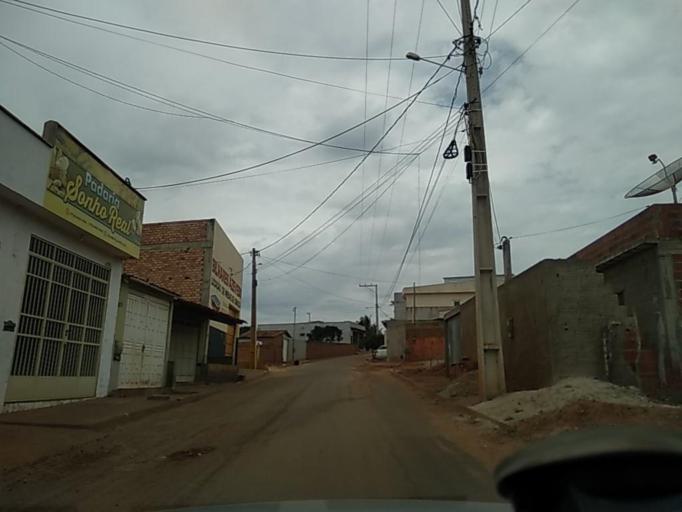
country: BR
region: Bahia
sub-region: Caetite
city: Caetite
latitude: -14.0526
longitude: -42.4766
